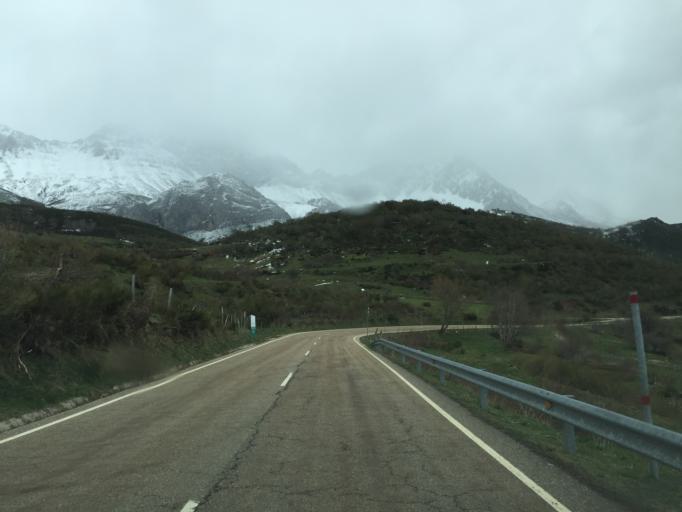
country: ES
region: Castille and Leon
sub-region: Provincia de Leon
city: San Emiliano
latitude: 43.0318
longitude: -6.0102
